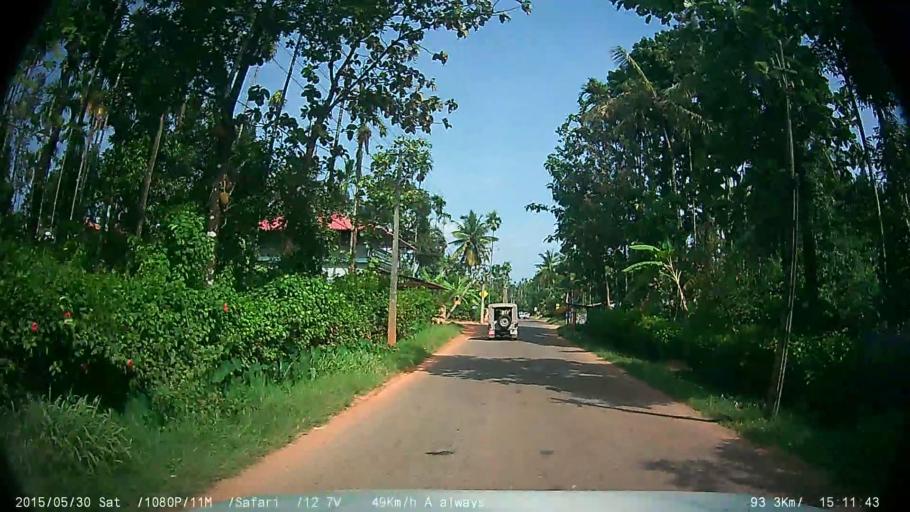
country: IN
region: Kerala
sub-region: Wayanad
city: Panamaram
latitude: 11.8005
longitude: 76.0373
